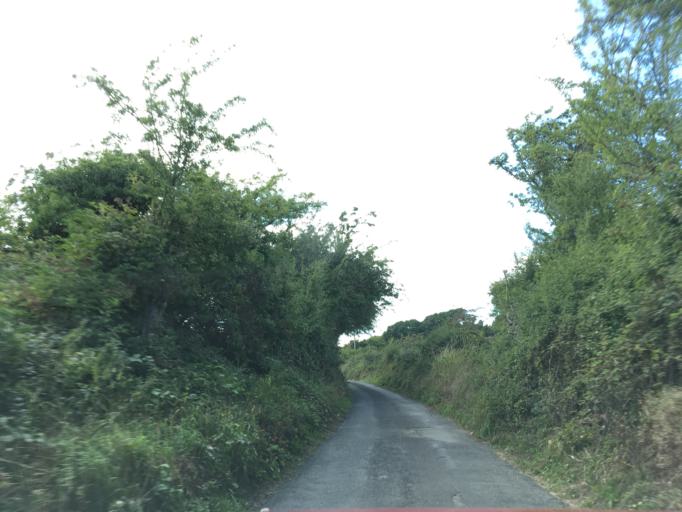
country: IE
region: Munster
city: Cashel
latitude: 52.5205
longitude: -7.8773
